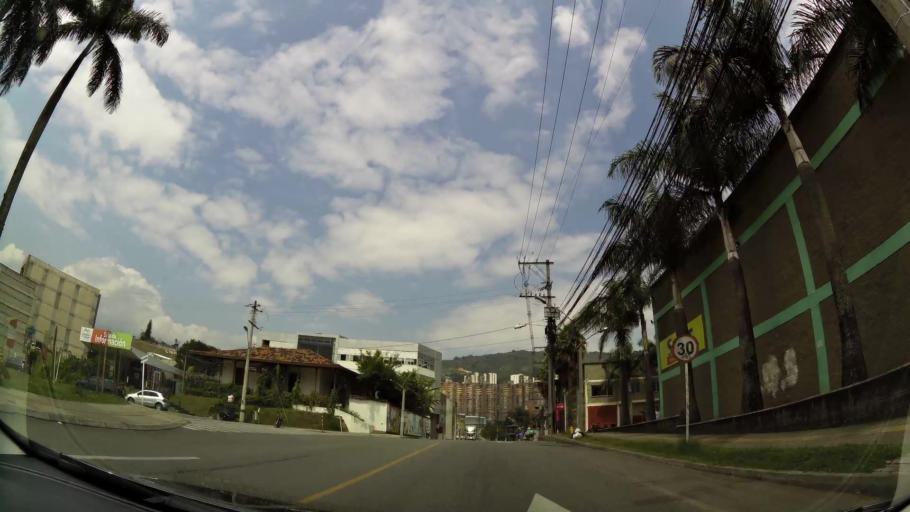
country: CO
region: Antioquia
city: Itagui
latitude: 6.1882
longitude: -75.5984
